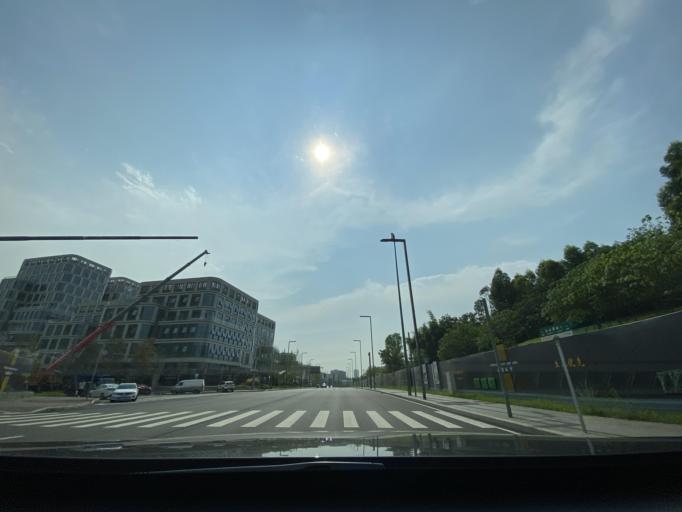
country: CN
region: Sichuan
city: Dongsheng
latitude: 30.3925
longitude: 104.0878
